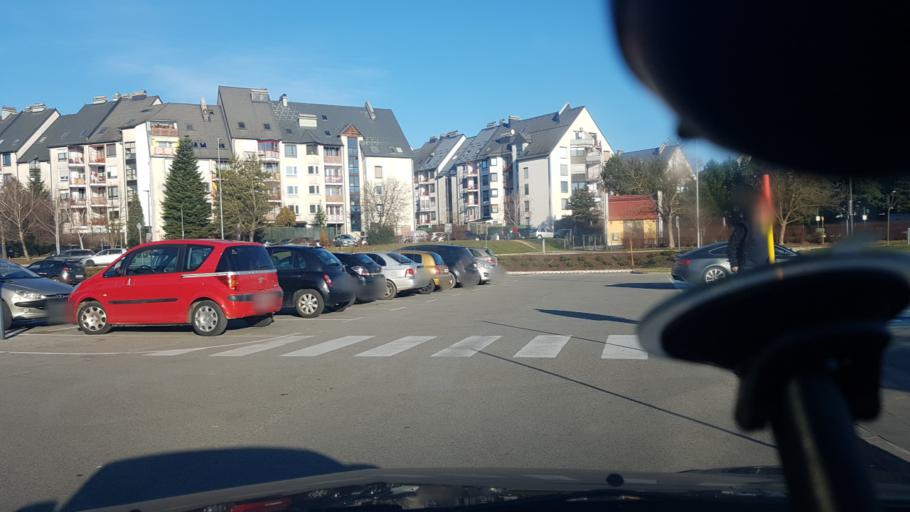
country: SI
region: Ptuj
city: Ptuj
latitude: 46.4278
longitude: 15.8679
